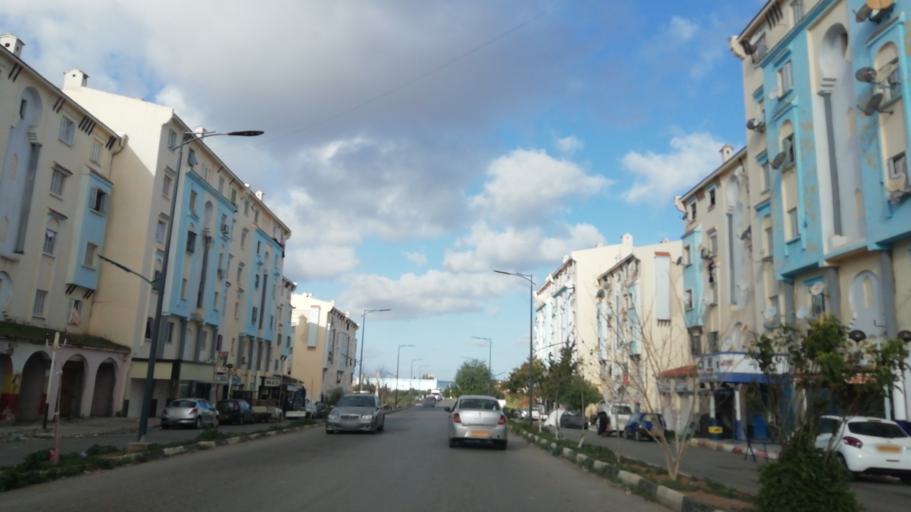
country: DZ
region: Ain Temouchent
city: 'Ain Temouchent
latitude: 35.3021
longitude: -1.1545
